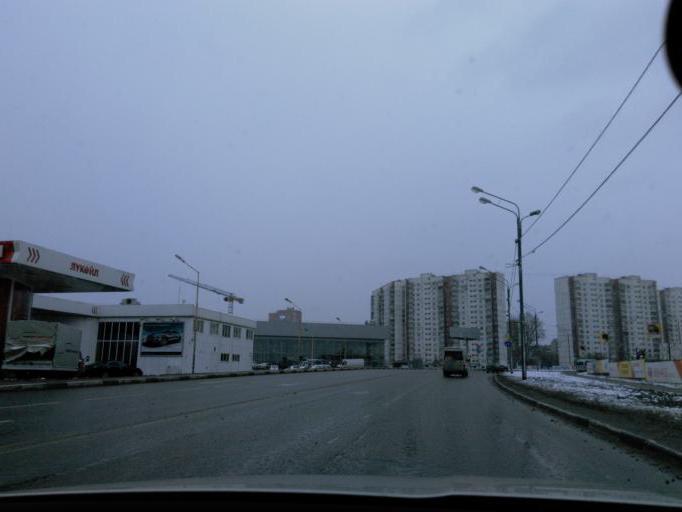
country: RU
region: Moscow
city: Khimki
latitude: 55.9093
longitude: 37.4067
